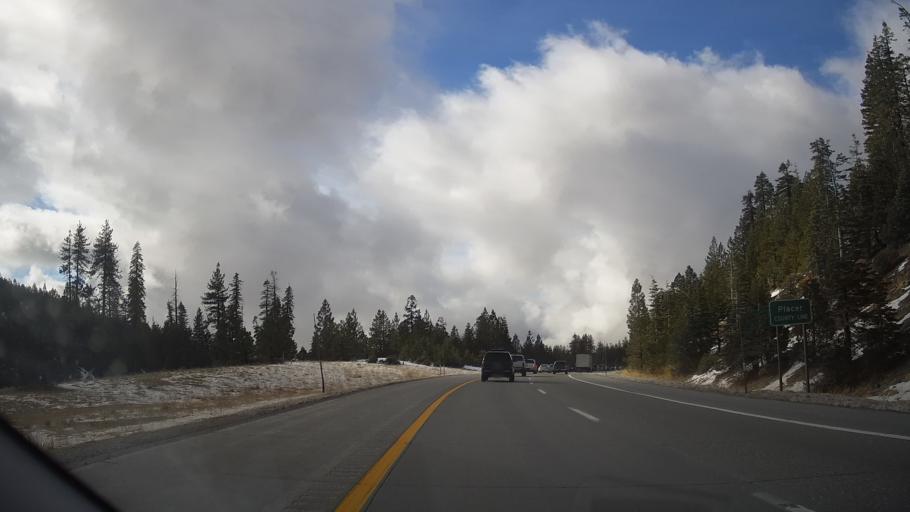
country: US
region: California
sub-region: Sierra County
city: Downieville
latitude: 39.3158
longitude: -120.6177
